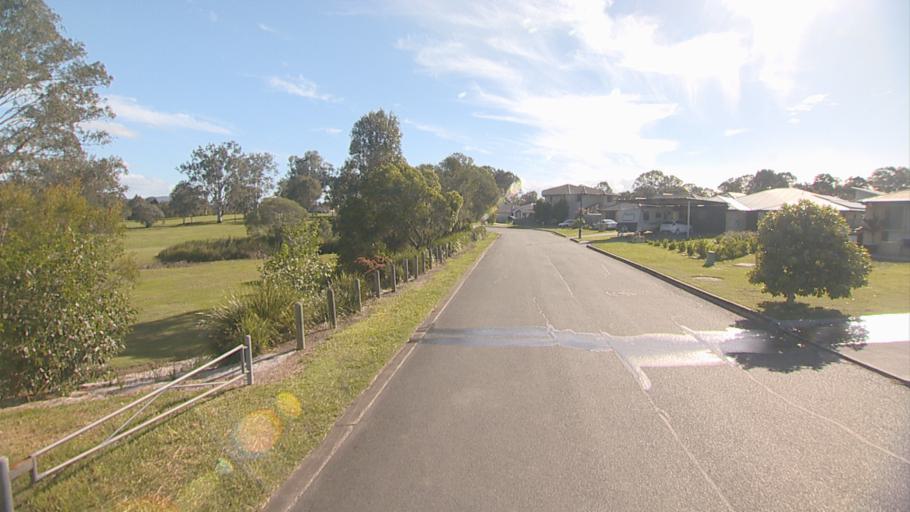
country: AU
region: Queensland
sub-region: Gold Coast
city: Yatala
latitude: -27.7056
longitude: 153.2280
